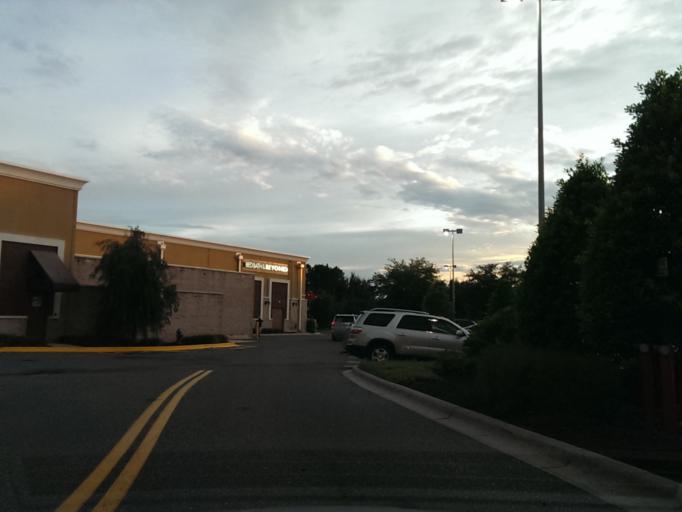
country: US
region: Florida
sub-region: Orange County
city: Winter Garden
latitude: 28.5241
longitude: -81.5849
